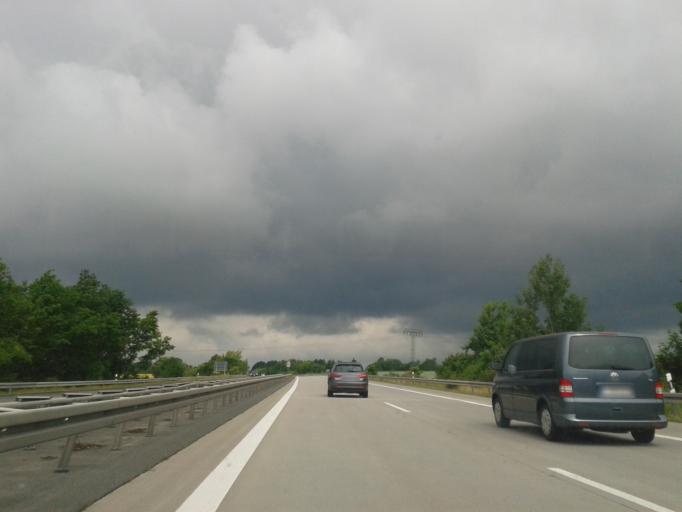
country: DE
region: Saxony
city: Nossen
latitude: 51.0640
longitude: 13.3321
